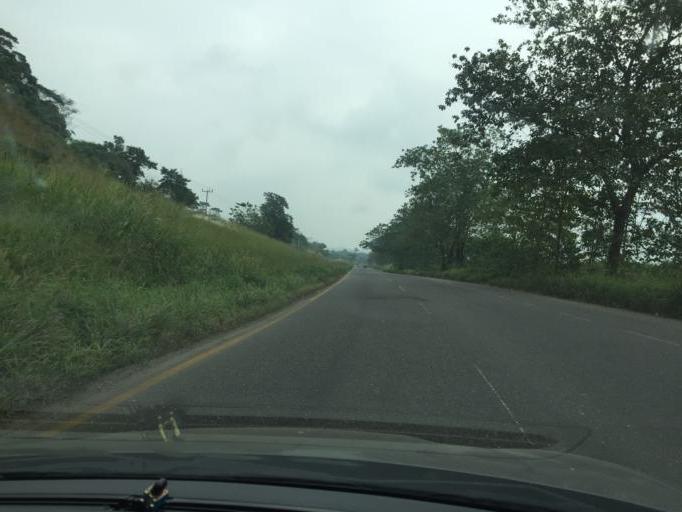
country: MX
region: Veracruz
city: Villa Nanchital
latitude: 18.0696
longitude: -94.3099
